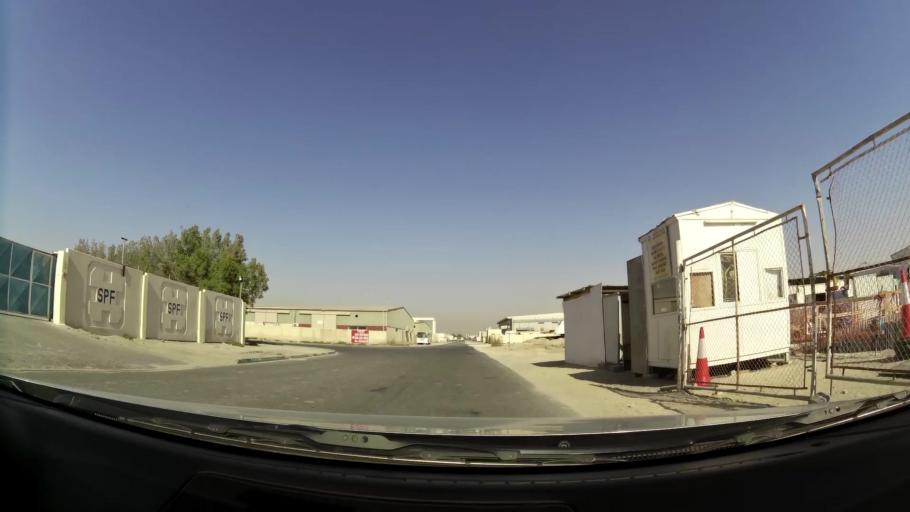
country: AE
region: Dubai
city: Dubai
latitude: 24.9861
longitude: 55.1079
